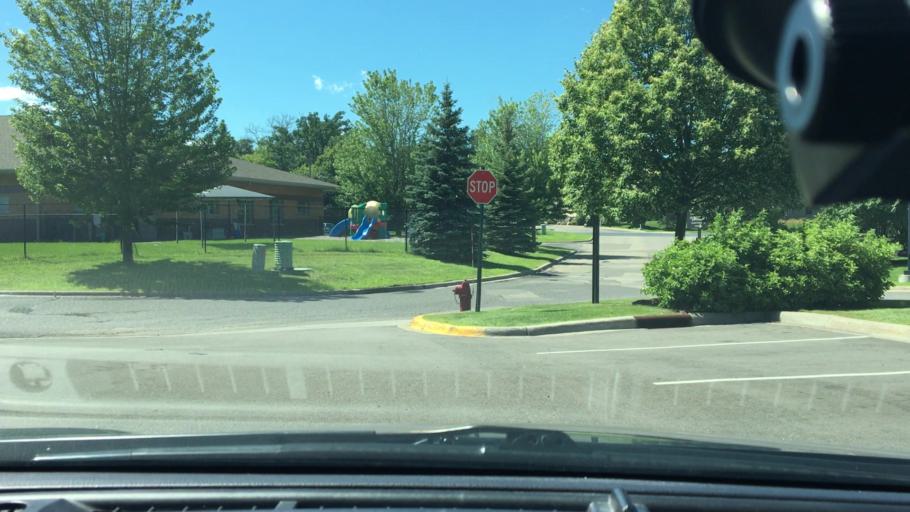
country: US
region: Minnesota
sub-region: Hennepin County
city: Maple Grove
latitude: 45.0703
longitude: -93.4485
